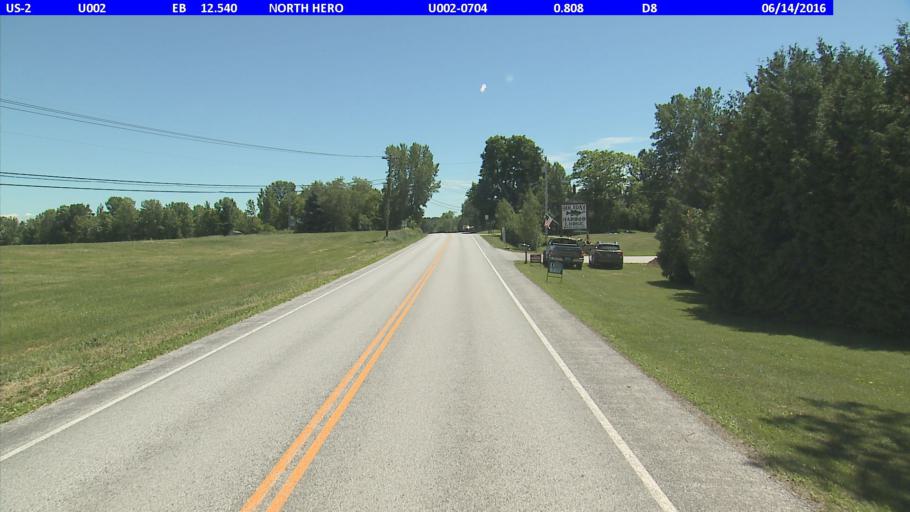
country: US
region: Vermont
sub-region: Grand Isle County
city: North Hero
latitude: 44.8748
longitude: -73.2715
